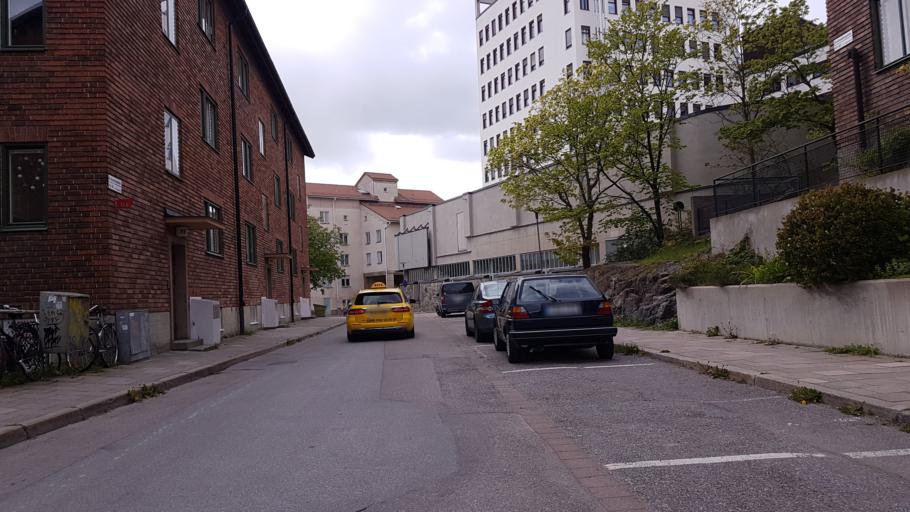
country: SE
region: Stockholm
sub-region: Stockholms Kommun
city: Arsta
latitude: 59.3159
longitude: 18.0451
